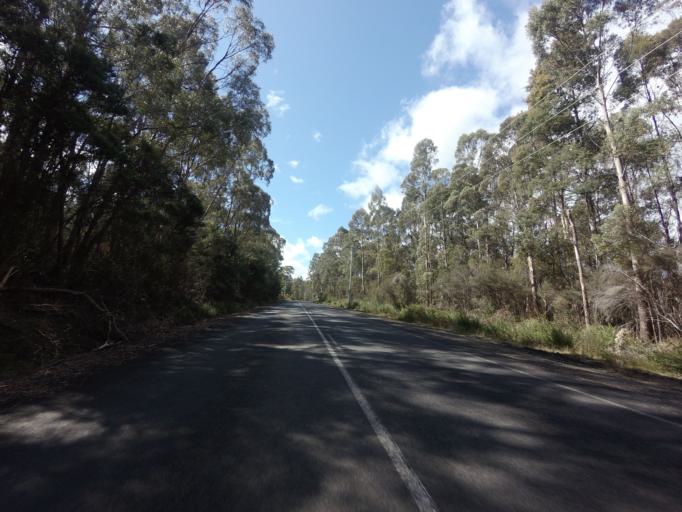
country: AU
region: Tasmania
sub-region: Huon Valley
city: Geeveston
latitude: -43.4137
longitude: 146.9394
